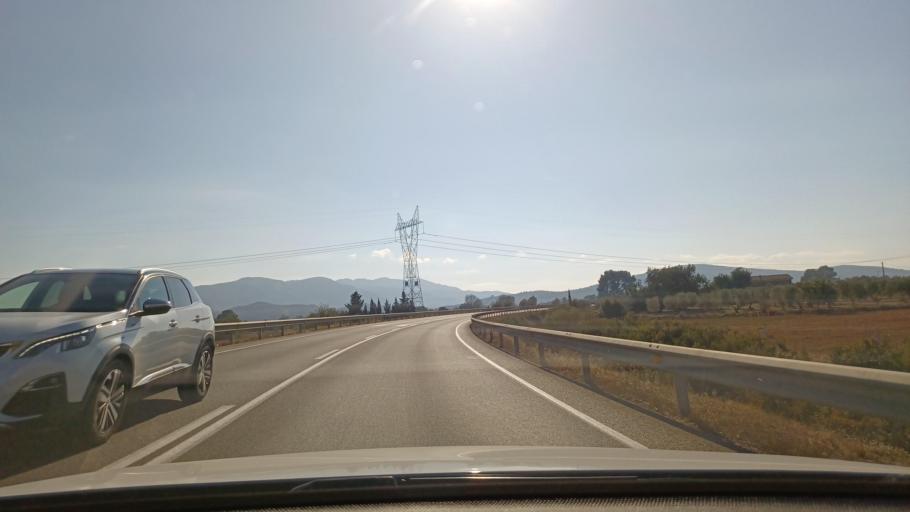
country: ES
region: Catalonia
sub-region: Provincia de Tarragona
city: Santa Barbara
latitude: 40.7120
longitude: 0.5069
